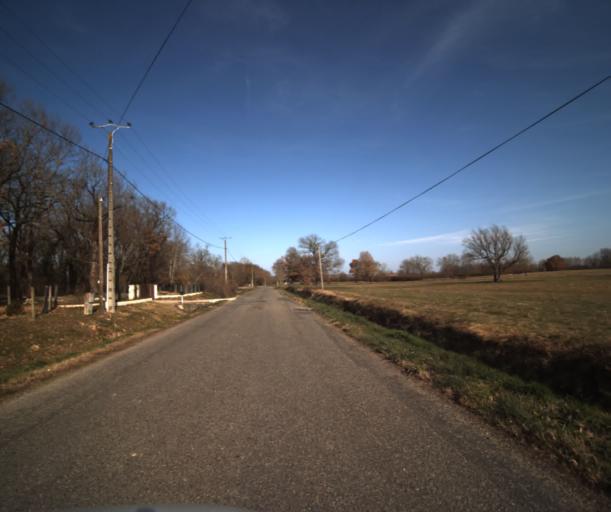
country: FR
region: Midi-Pyrenees
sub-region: Departement du Tarn-et-Garonne
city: Campsas
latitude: 43.9249
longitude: 1.3201
